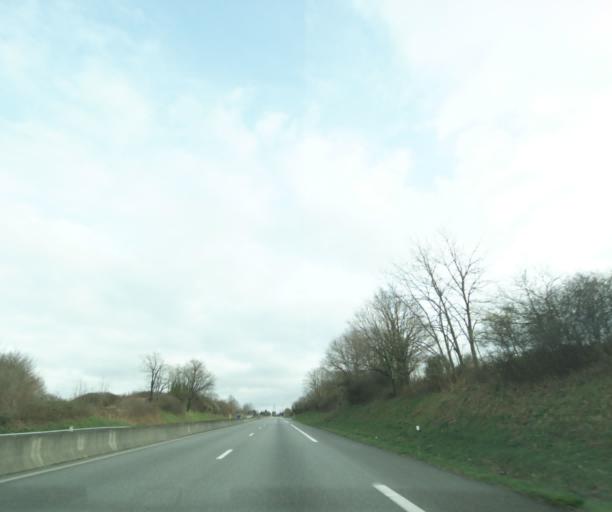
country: FR
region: Limousin
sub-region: Departement de la Haute-Vienne
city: Pierre-Buffiere
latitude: 45.7190
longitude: 1.3524
